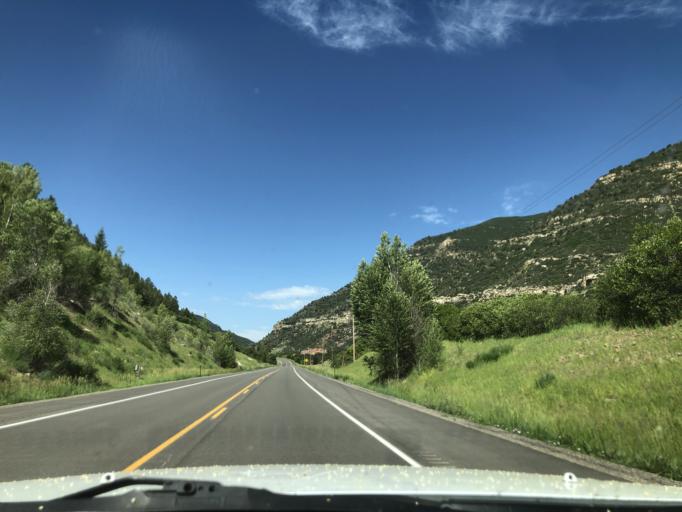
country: US
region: Colorado
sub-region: Delta County
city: Paonia
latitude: 38.9307
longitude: -107.4108
